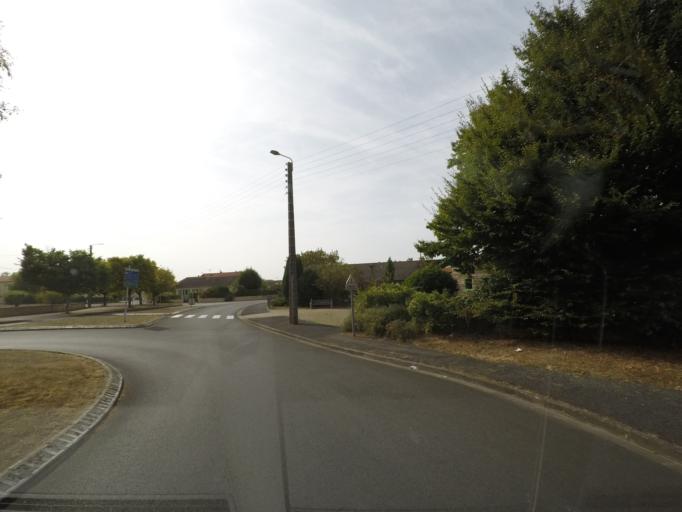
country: FR
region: Poitou-Charentes
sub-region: Departement des Deux-Sevres
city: Melle
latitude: 46.2306
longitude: -0.1357
